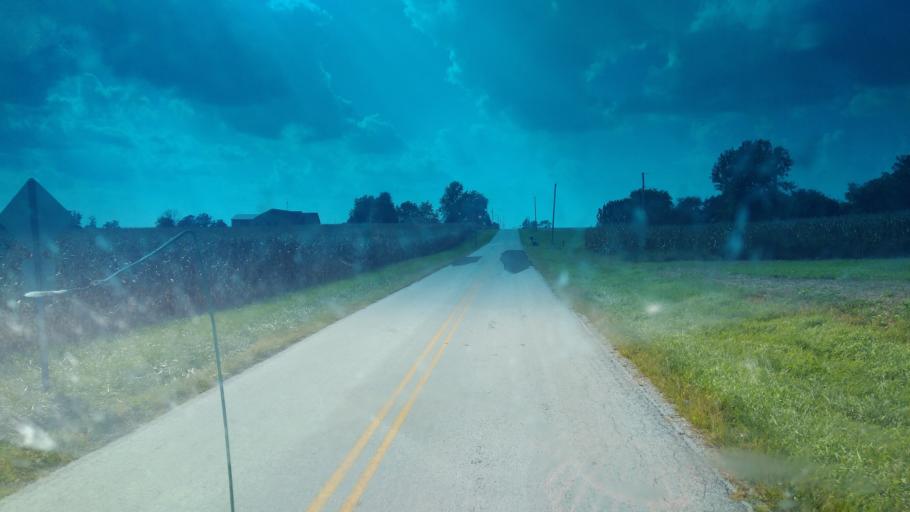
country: US
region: Ohio
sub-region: Hardin County
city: Kenton
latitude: 40.7465
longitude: -83.6444
